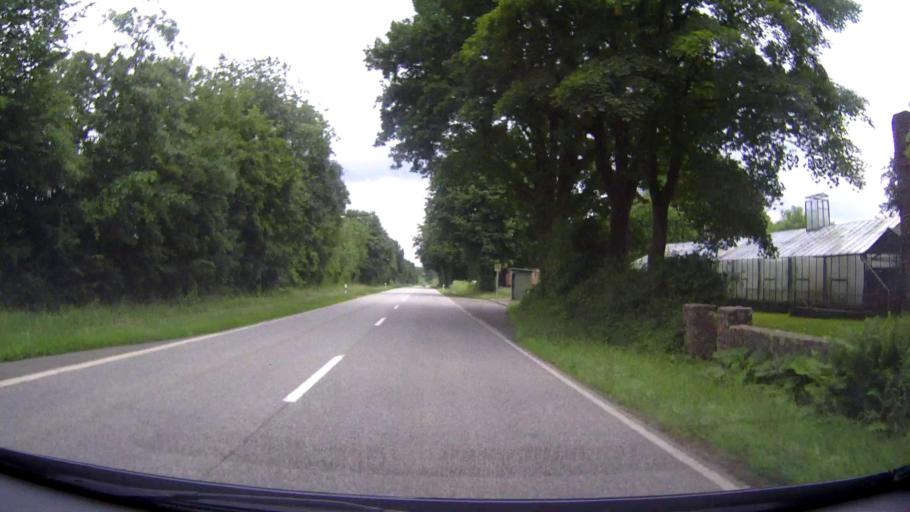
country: DE
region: Schleswig-Holstein
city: Warringholz
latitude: 54.0718
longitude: 9.4675
